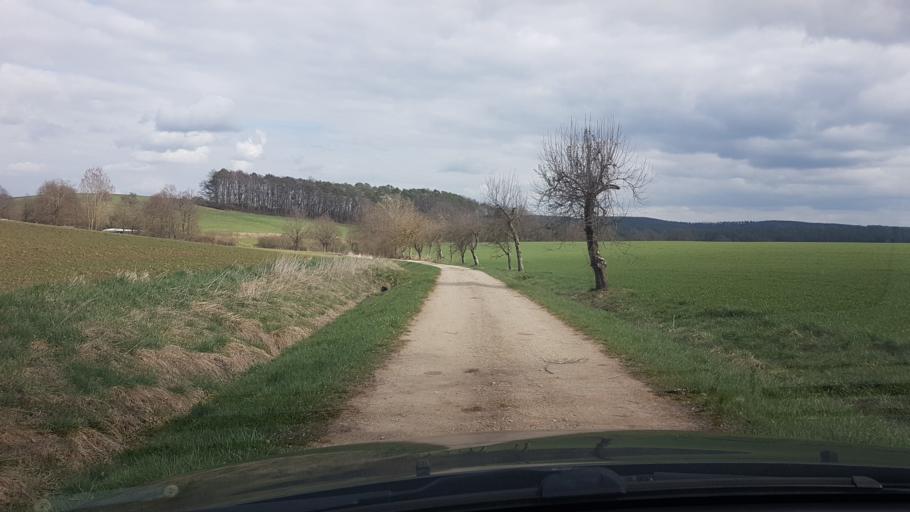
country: DE
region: Bavaria
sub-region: Upper Franconia
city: Pettstadt
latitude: 49.8009
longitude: 10.9106
